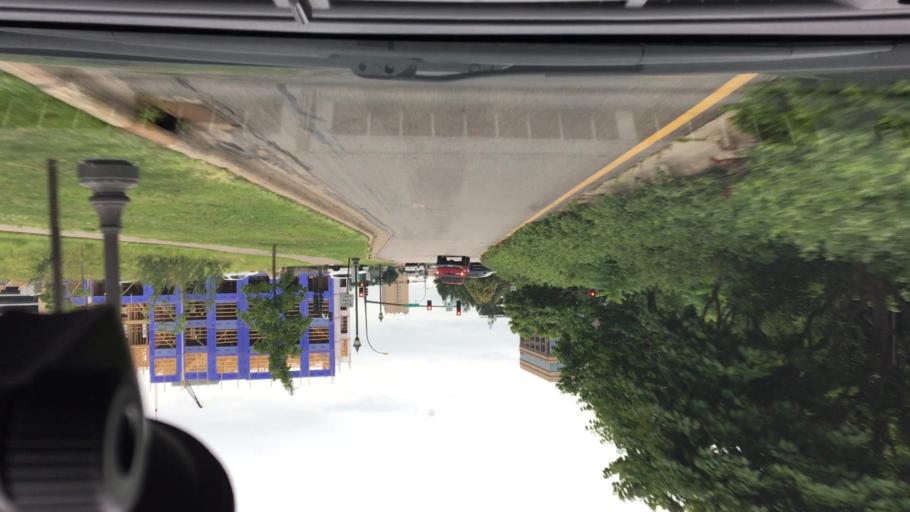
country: US
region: Minnesota
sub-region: Hennepin County
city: Saint Louis Park
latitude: 44.9756
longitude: -93.3525
